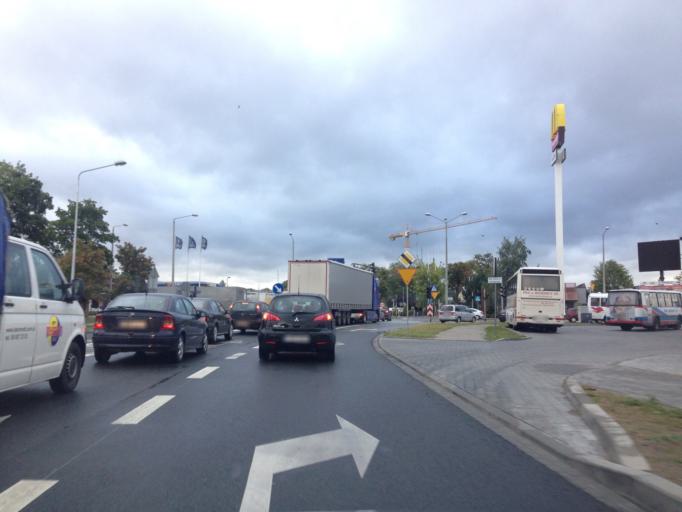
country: PL
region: Kujawsko-Pomorskie
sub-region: Powiat brodnicki
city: Brodnica
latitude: 53.2593
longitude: 19.3960
